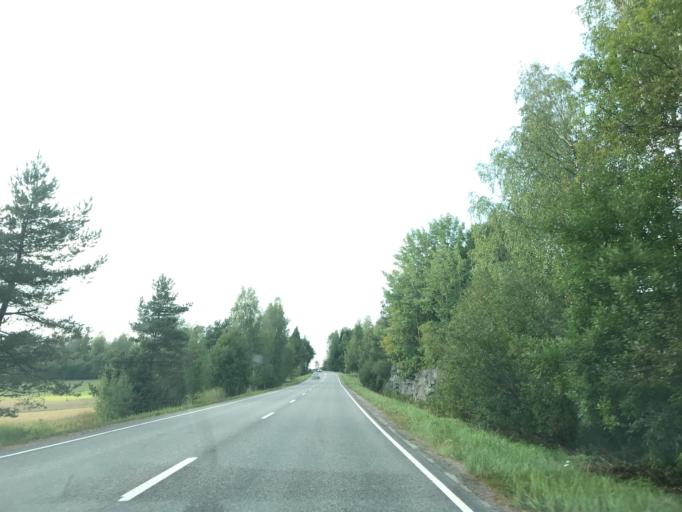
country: FI
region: Uusimaa
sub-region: Helsinki
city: Espoo
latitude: 60.1964
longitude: 24.5597
